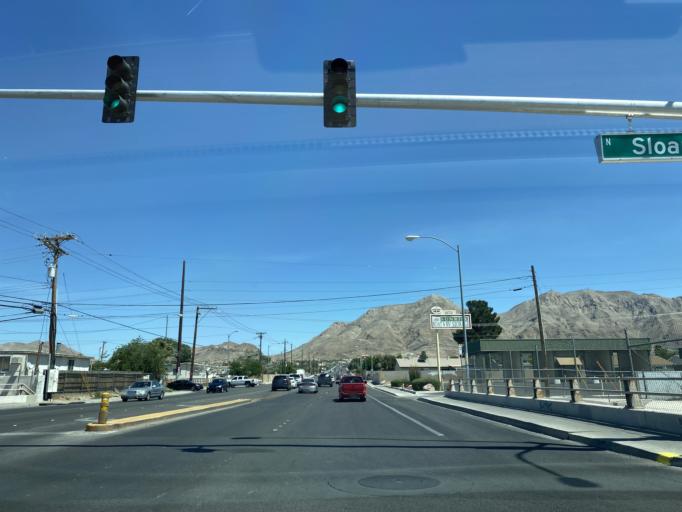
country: US
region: Nevada
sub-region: Clark County
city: Sunrise Manor
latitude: 36.1962
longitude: -115.0440
